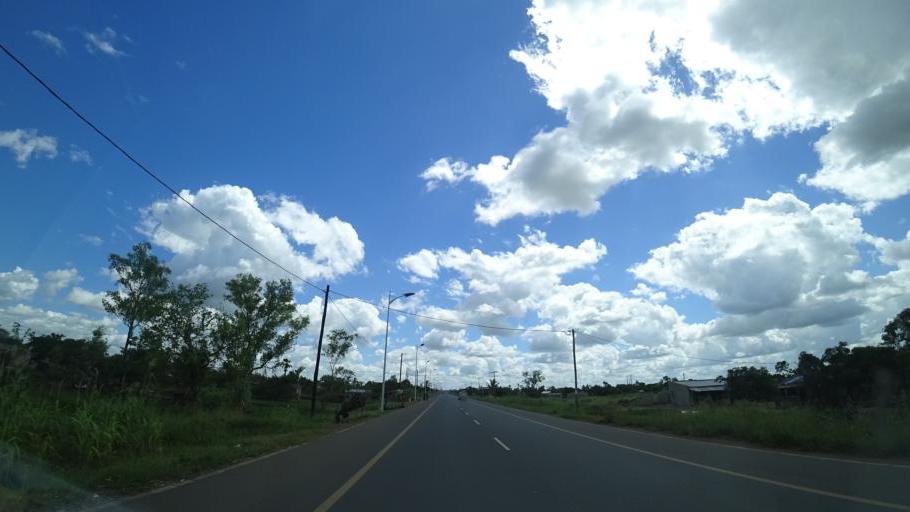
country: MZ
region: Sofala
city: Dondo
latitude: -19.2776
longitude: 34.2171
